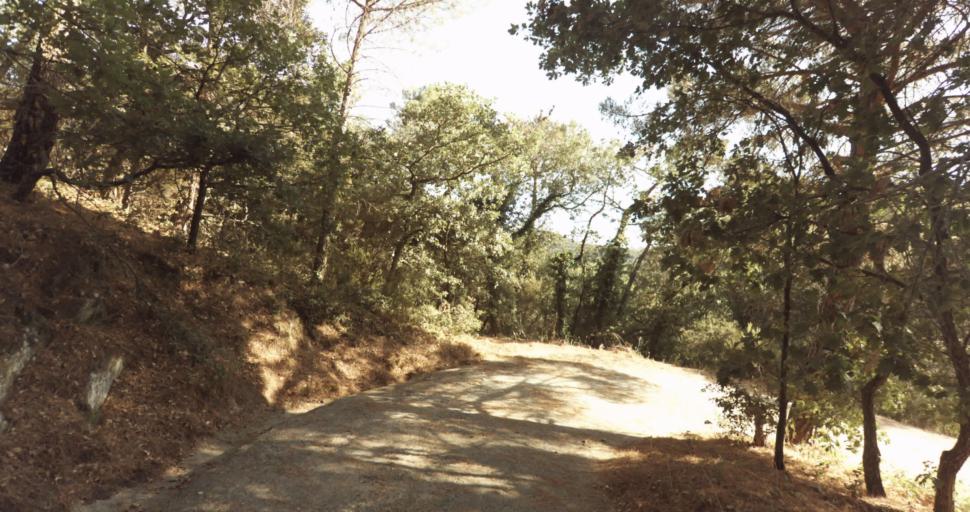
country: FR
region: Provence-Alpes-Cote d'Azur
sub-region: Departement du Var
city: Gassin
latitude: 43.2267
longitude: 6.5807
